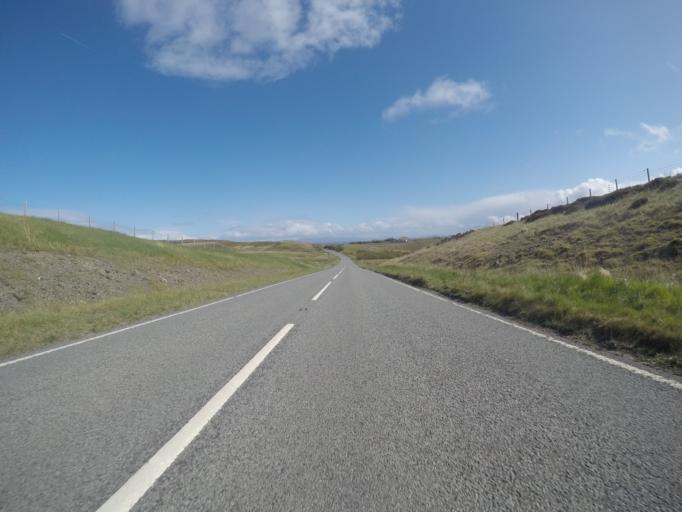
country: GB
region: Scotland
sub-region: Highland
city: Portree
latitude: 57.6170
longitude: -6.1912
